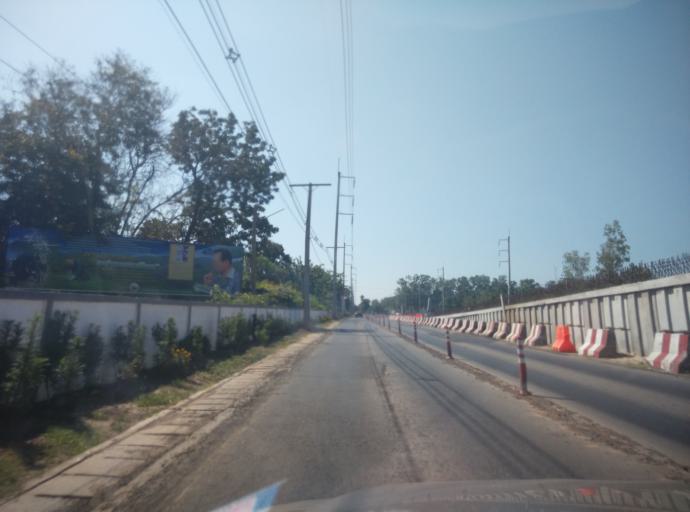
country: TH
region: Sisaket
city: Si Sa Ket
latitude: 15.1197
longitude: 104.2847
